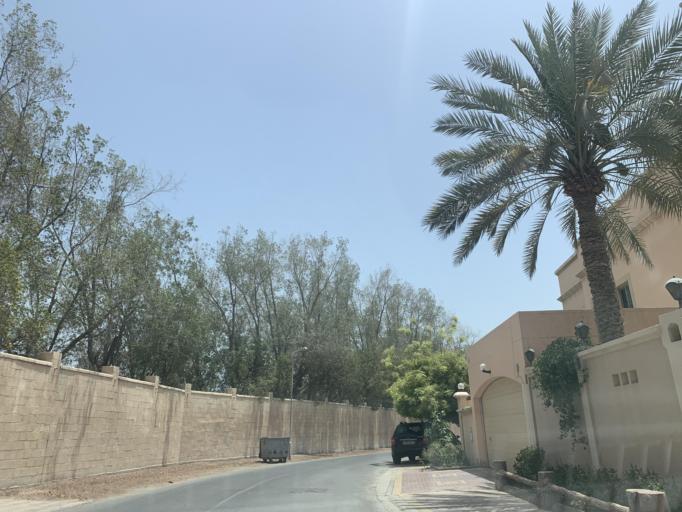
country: BH
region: Northern
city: Madinat `Isa
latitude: 26.1738
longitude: 50.5682
